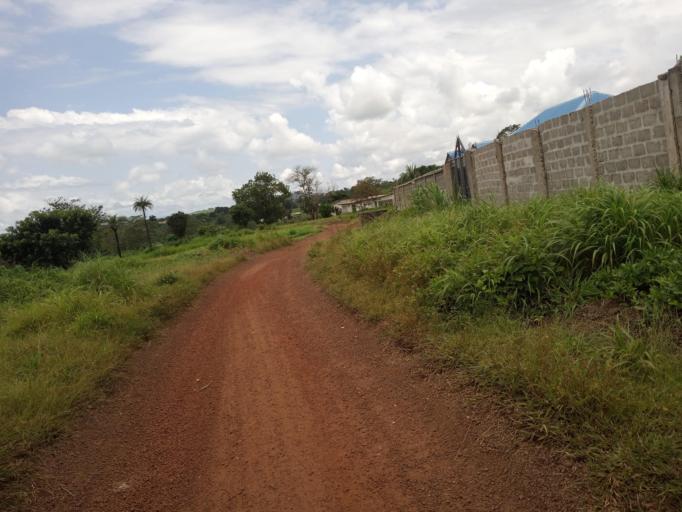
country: SL
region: Northern Province
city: Kamakwie
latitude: 9.4855
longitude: -12.2438
